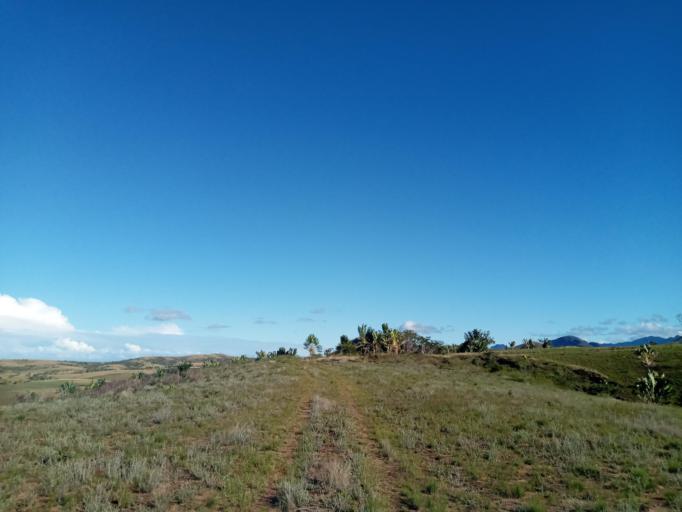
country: MG
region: Anosy
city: Fort Dauphin
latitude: -24.4066
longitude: 47.2548
